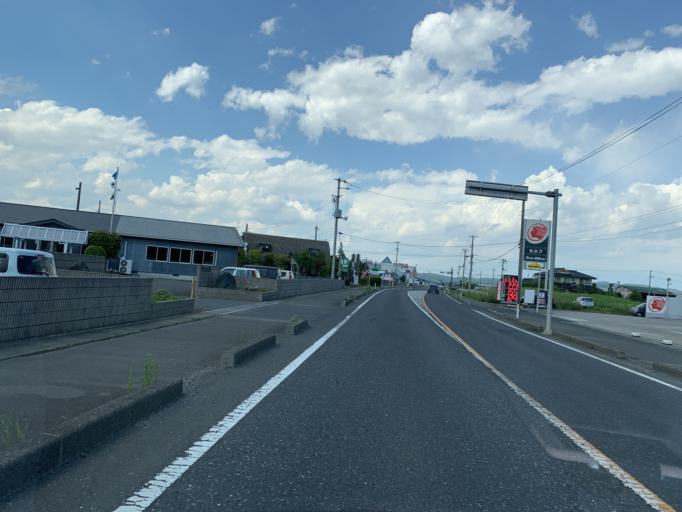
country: JP
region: Miyagi
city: Wakuya
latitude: 38.5069
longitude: 141.1206
